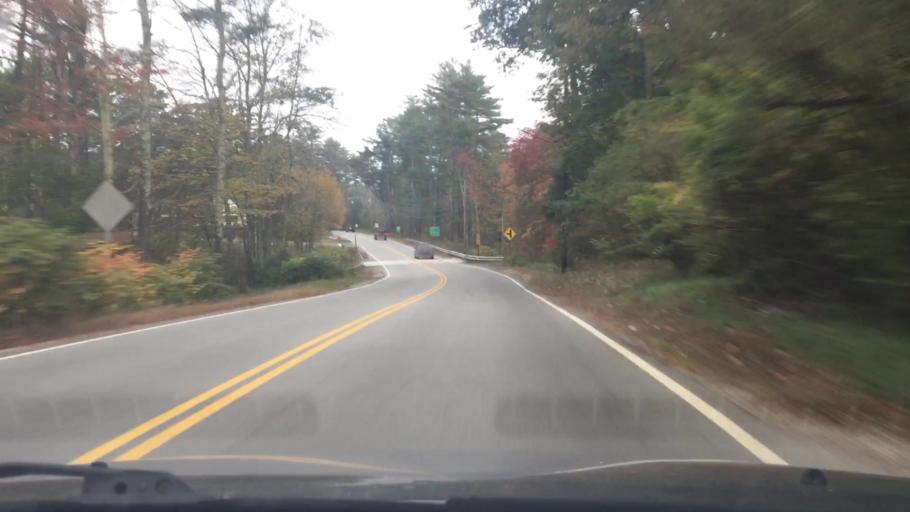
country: US
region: New Hampshire
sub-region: Cheshire County
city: Swanzey
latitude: 42.8454
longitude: -72.2788
